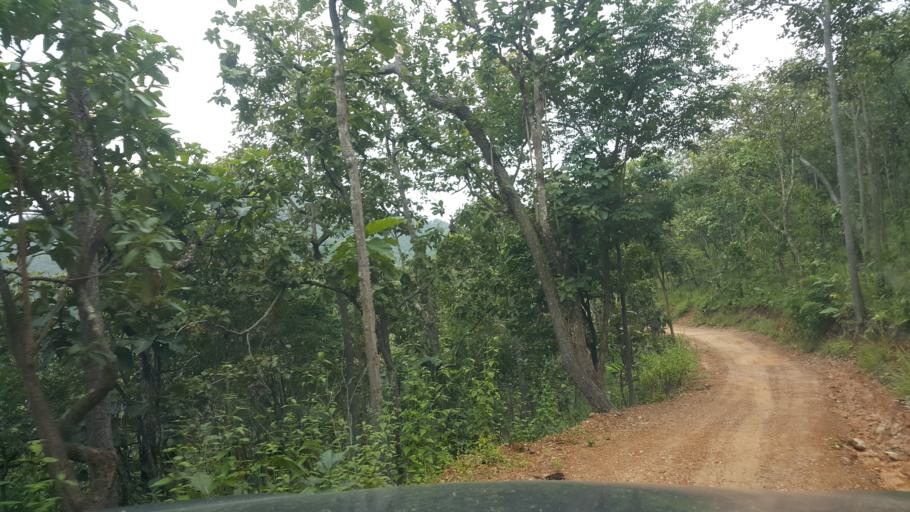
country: TH
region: Chiang Mai
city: San Sai
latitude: 18.9571
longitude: 99.1314
